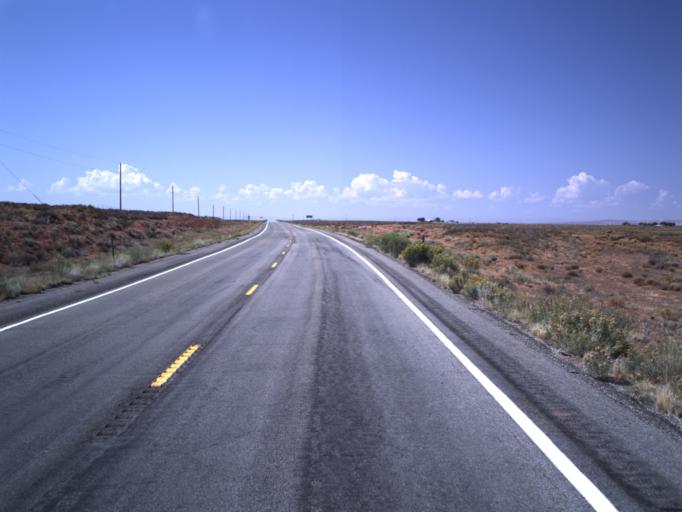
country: US
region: Utah
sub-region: San Juan County
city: Blanding
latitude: 37.0270
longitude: -109.6002
